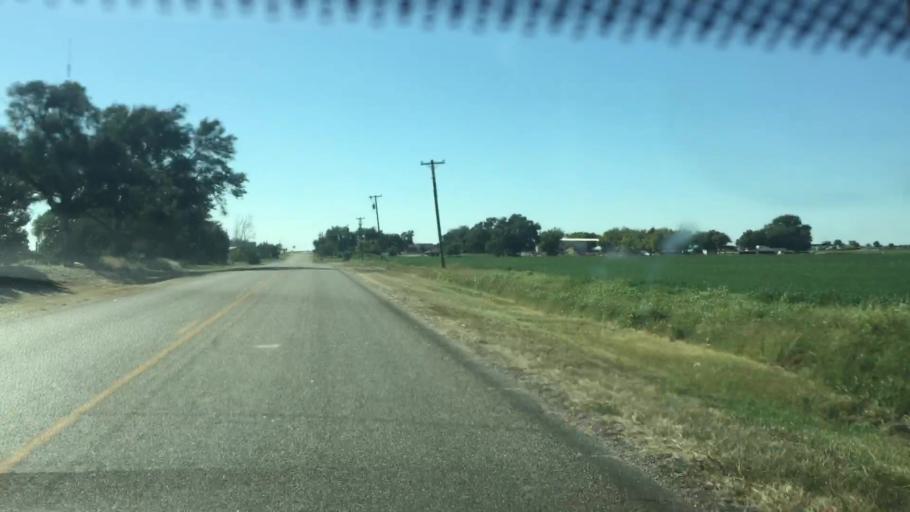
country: US
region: Colorado
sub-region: Prowers County
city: Lamar
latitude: 38.1168
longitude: -102.6150
